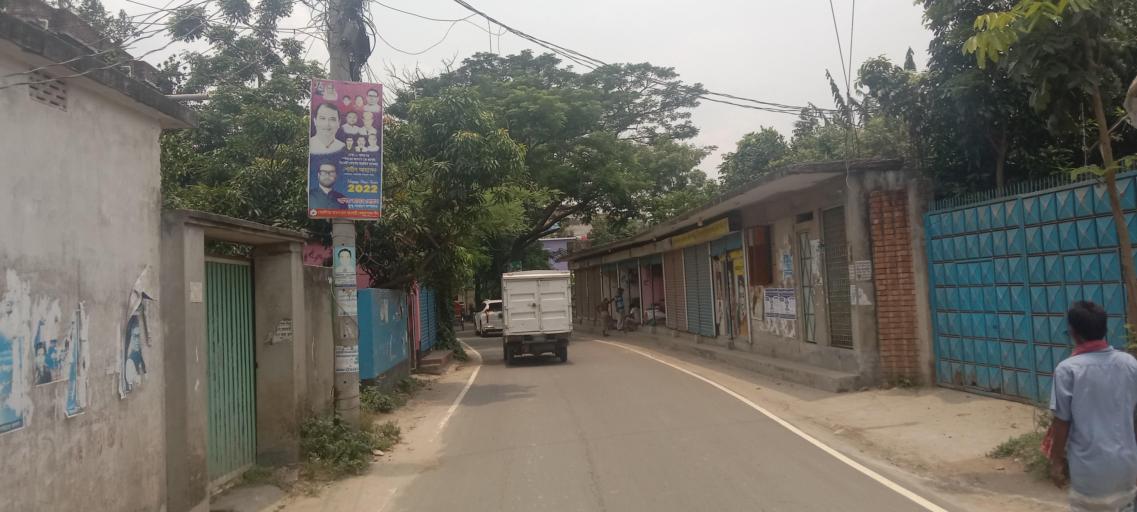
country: BD
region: Dhaka
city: Azimpur
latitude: 23.7178
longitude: 90.3449
